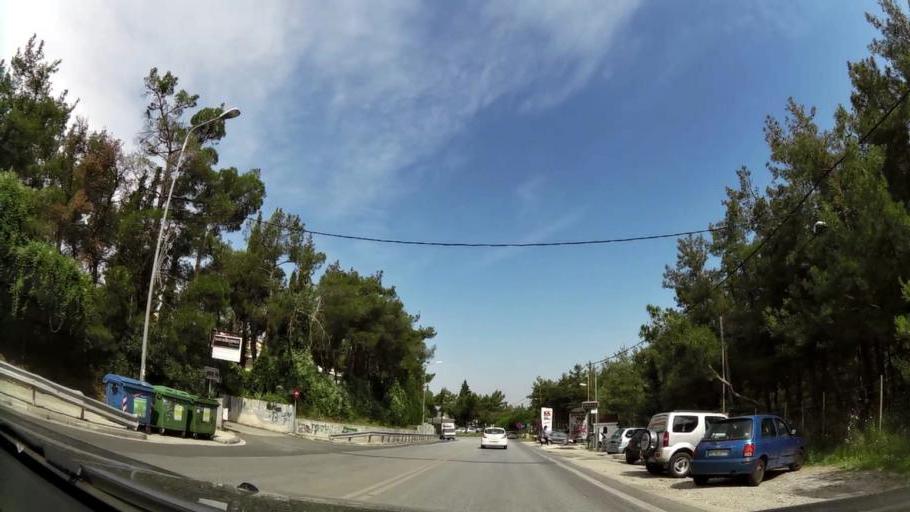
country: GR
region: Central Macedonia
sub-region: Nomos Thessalonikis
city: Panorama
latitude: 40.5922
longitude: 23.0169
